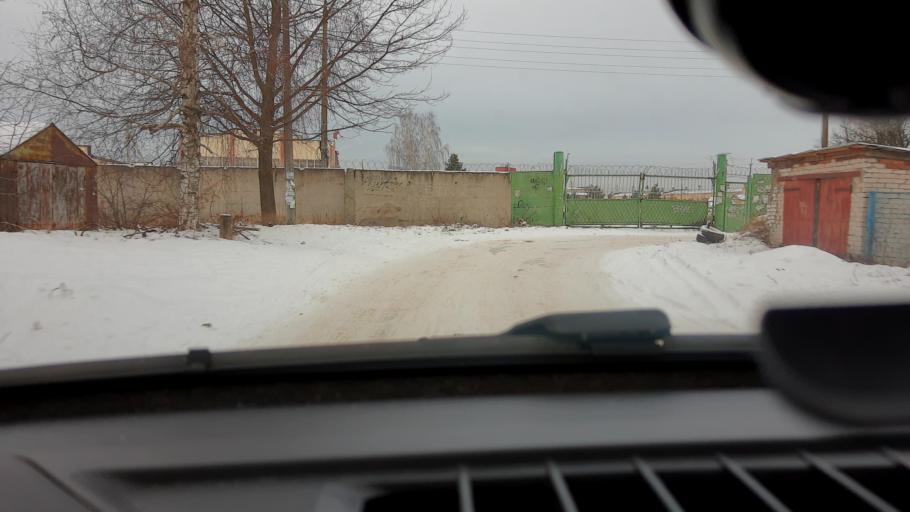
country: RU
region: Nizjnij Novgorod
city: Gorbatovka
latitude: 56.3723
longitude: 43.8242
